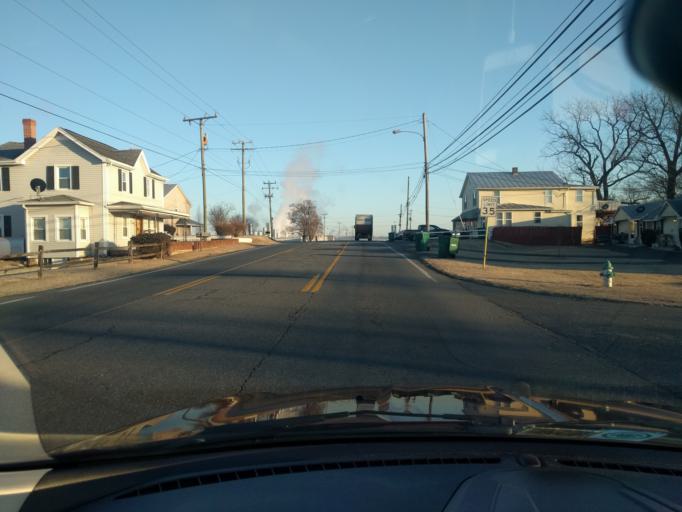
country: US
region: Virginia
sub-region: Rockingham County
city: Bridgewater
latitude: 38.3623
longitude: -78.9376
